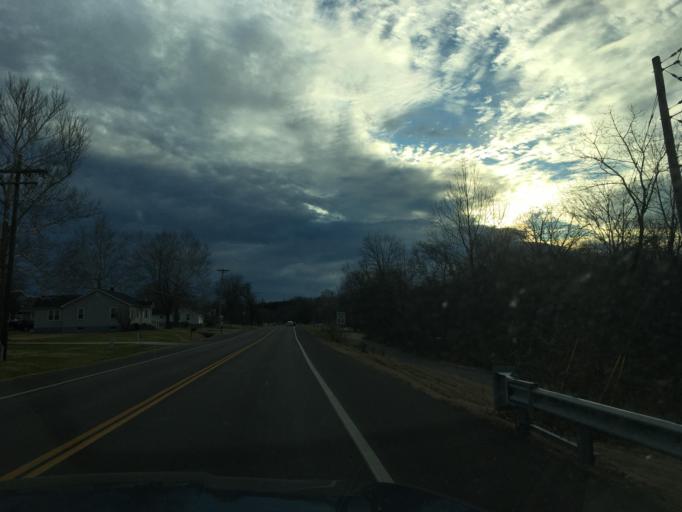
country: US
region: Missouri
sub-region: Jefferson County
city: De Soto
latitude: 38.1266
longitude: -90.5565
